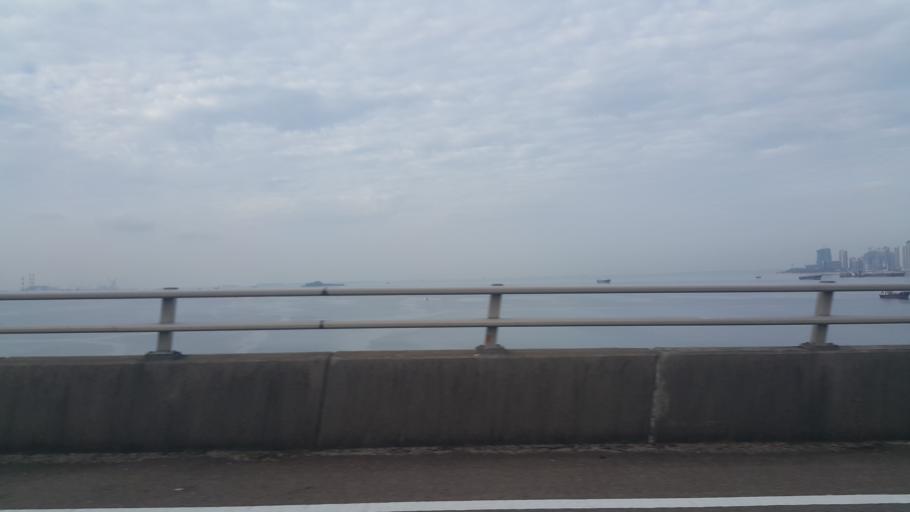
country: MY
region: Johor
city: Johor Bahru
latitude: 1.3532
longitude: 103.6299
